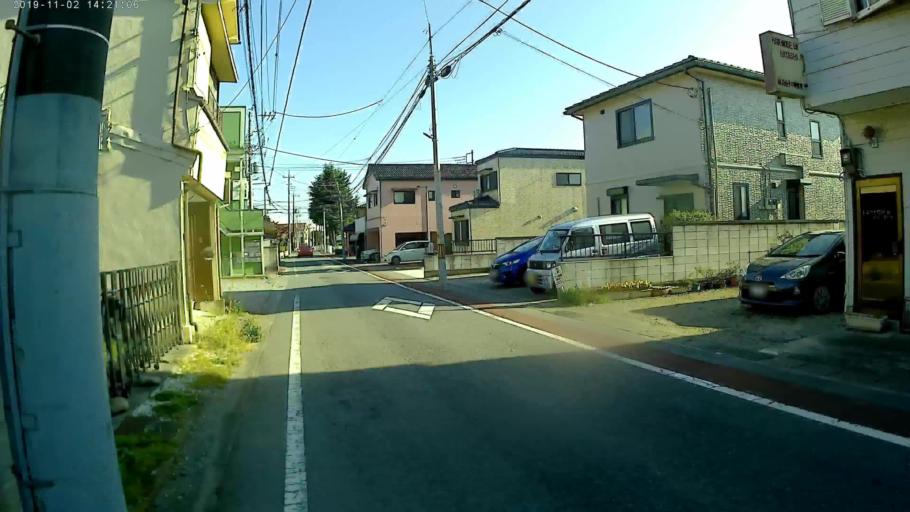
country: JP
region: Gunma
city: Takasaki
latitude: 36.3321
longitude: 138.9938
